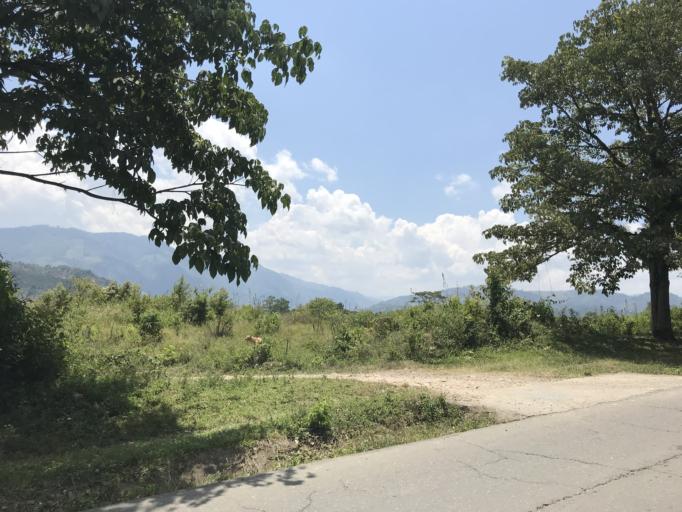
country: CO
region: Huila
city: San Agustin
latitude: 1.8761
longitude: -76.2520
